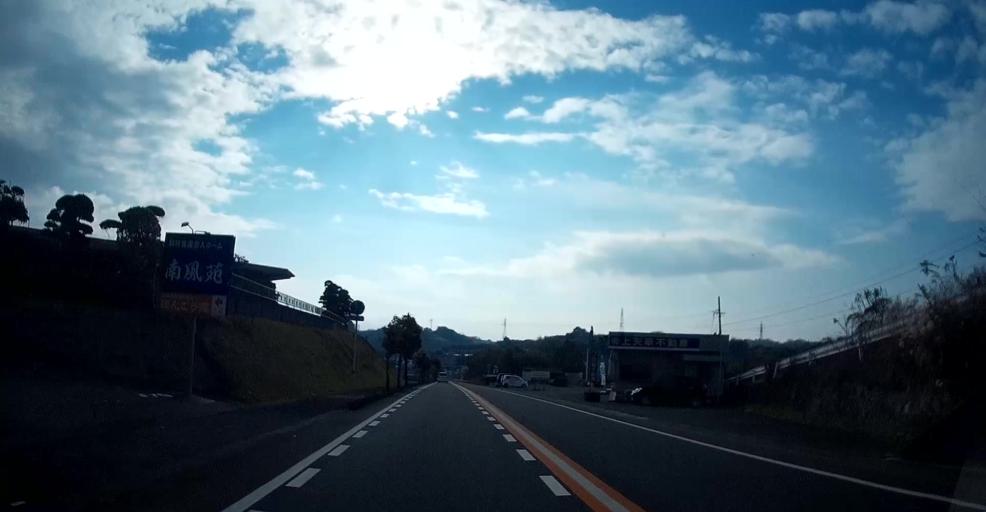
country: JP
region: Kumamoto
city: Yatsushiro
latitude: 32.5942
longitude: 130.4325
